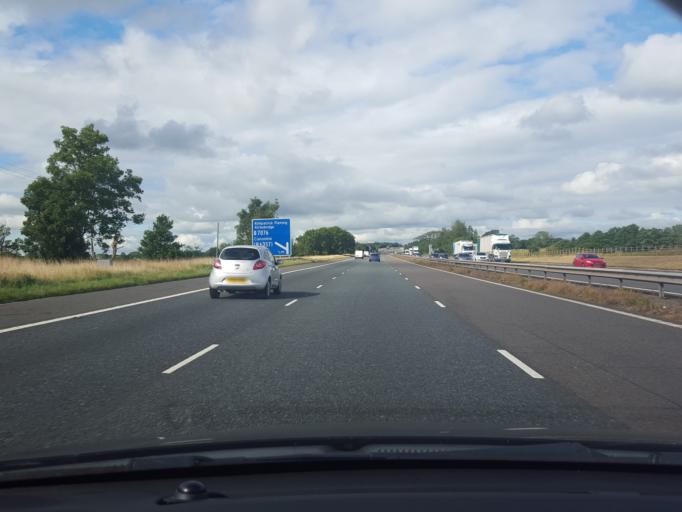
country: GB
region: Scotland
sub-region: Dumfries and Galloway
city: Gretna
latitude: 55.0135
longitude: -3.1024
